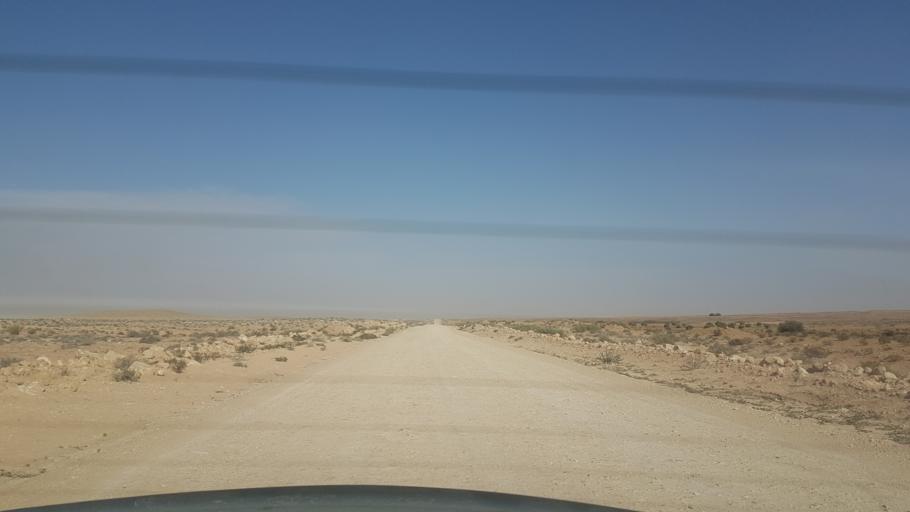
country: TN
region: Qabis
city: El Hamma
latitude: 33.6645
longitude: 9.7354
